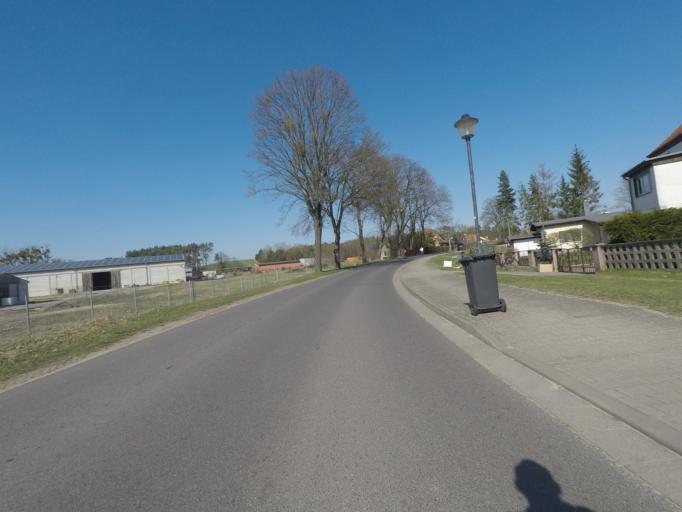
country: DE
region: Brandenburg
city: Marienwerder
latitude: 52.8571
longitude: 13.6812
